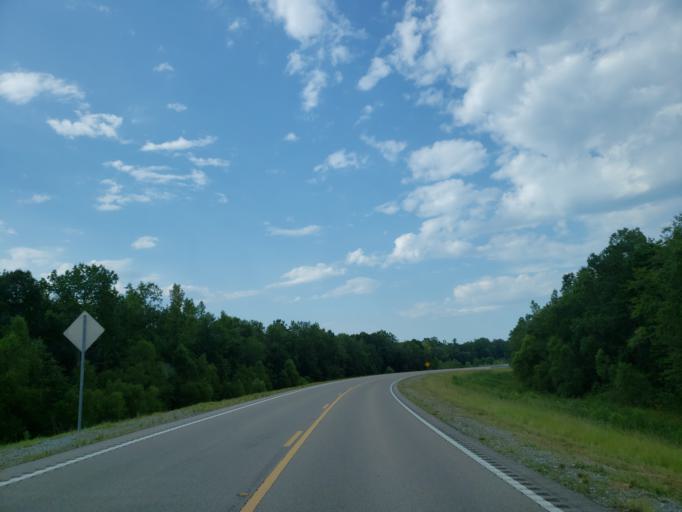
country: US
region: Mississippi
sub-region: Clarke County
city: Stonewall
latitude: 32.1746
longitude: -88.9291
